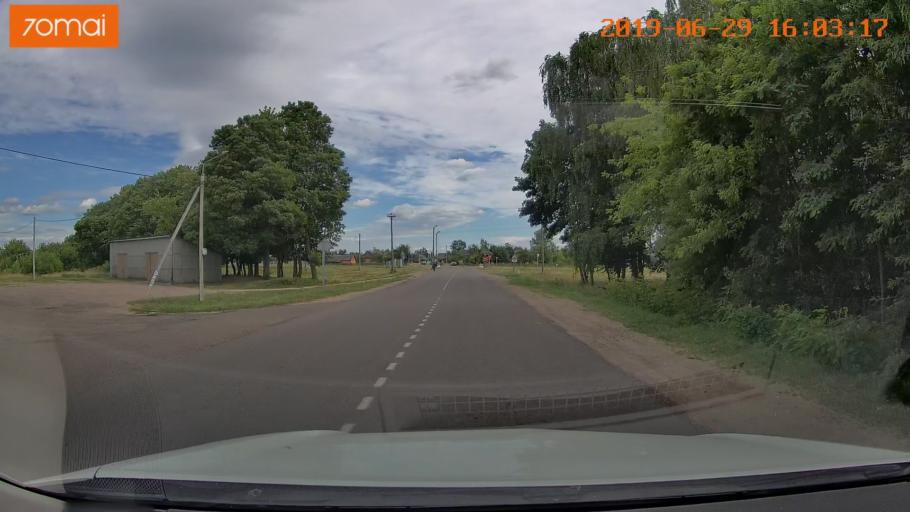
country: BY
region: Brest
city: Luninyets
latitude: 52.2298
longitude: 27.0189
